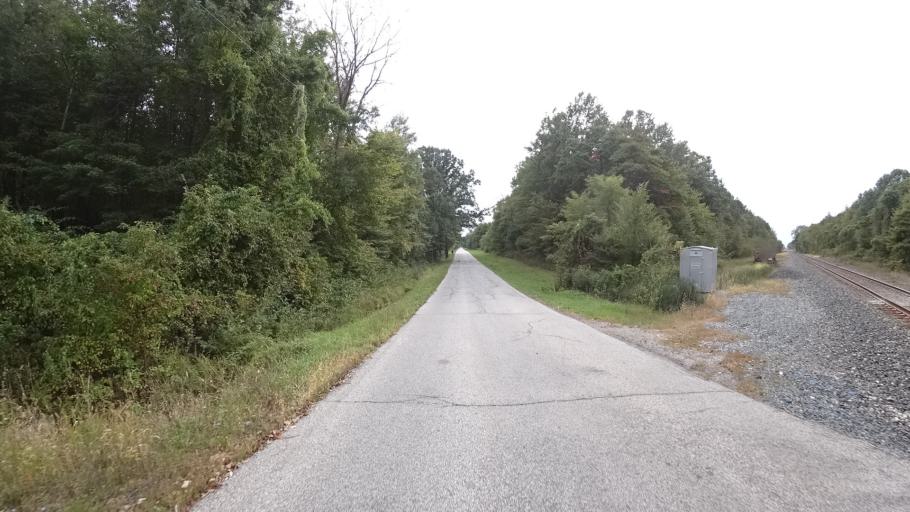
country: US
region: Indiana
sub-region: LaPorte County
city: Long Beach
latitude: 41.7375
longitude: -86.8161
